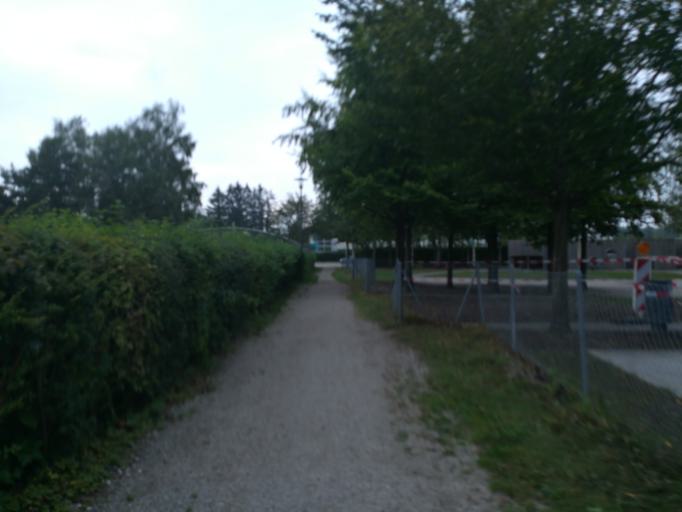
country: DE
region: Bavaria
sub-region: Upper Bavaria
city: Karlsfeld
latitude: 48.2265
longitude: 11.4792
